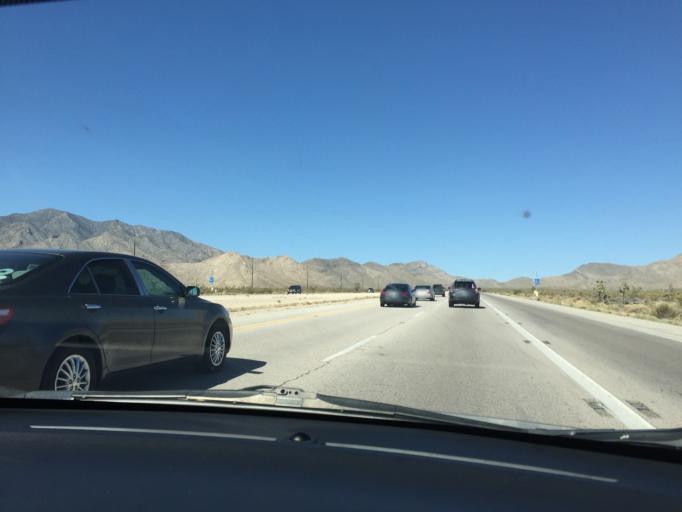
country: US
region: Nevada
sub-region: Clark County
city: Sandy Valley
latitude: 35.4590
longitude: -115.6312
